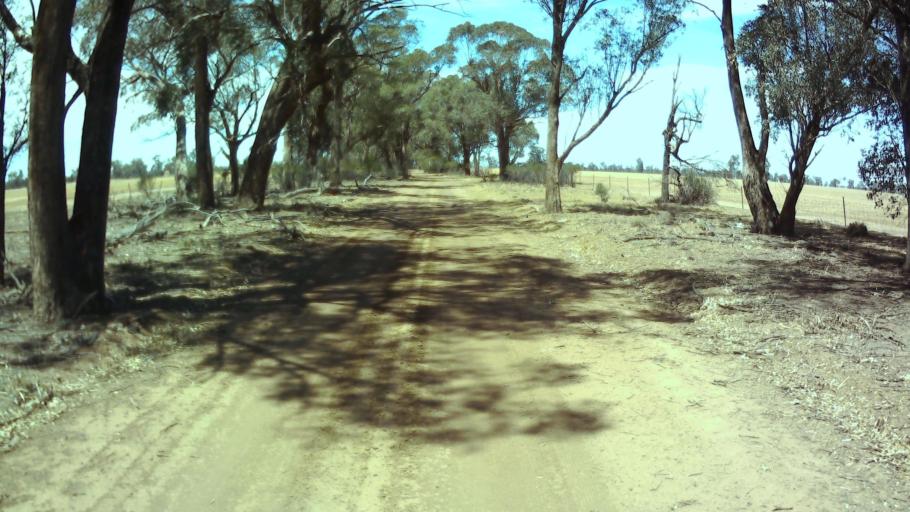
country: AU
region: New South Wales
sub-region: Weddin
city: Grenfell
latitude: -33.9162
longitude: 147.8056
